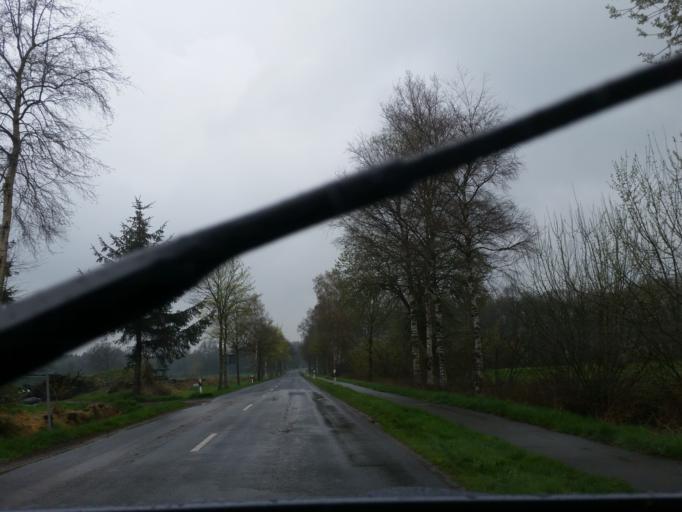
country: DE
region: Lower Saxony
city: Hipstedt
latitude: 53.4841
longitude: 8.9683
